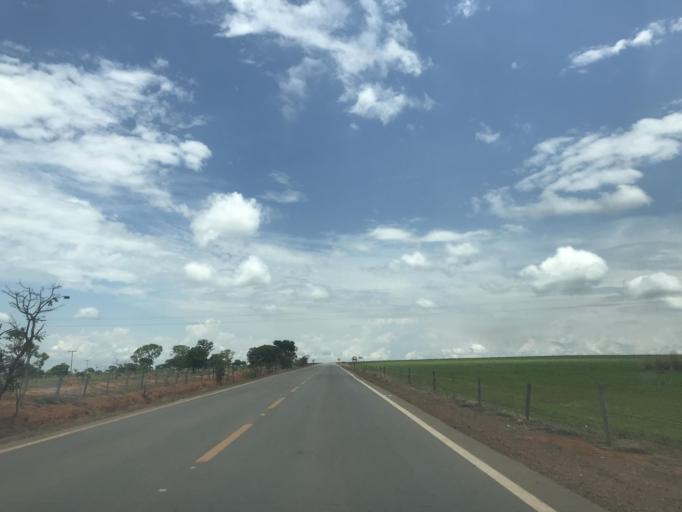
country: BR
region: Goias
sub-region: Luziania
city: Luziania
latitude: -16.3892
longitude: -48.1478
